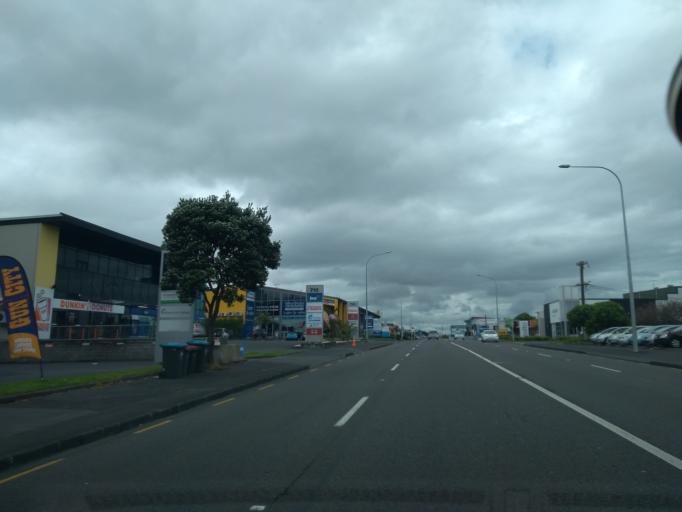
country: NZ
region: Auckland
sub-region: Auckland
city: Tamaki
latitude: -36.9052
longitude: 174.8099
